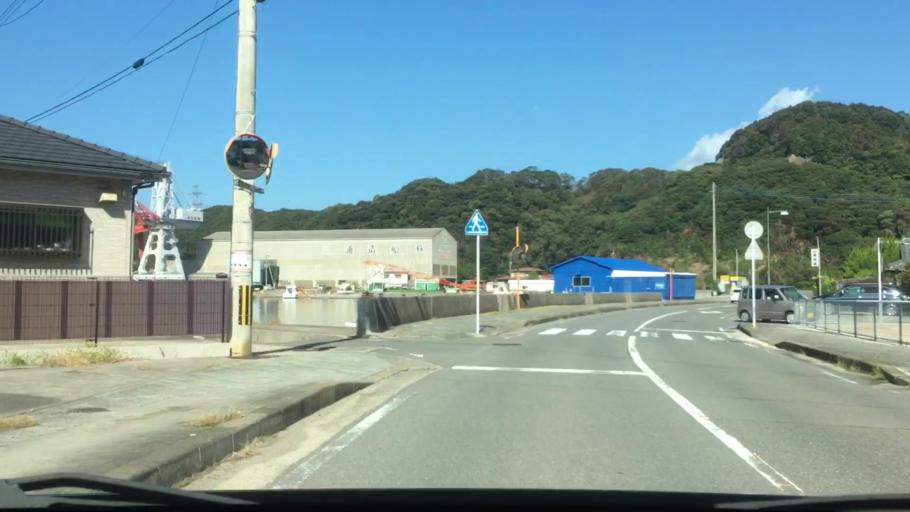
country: JP
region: Nagasaki
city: Sasebo
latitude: 32.9455
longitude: 129.6380
